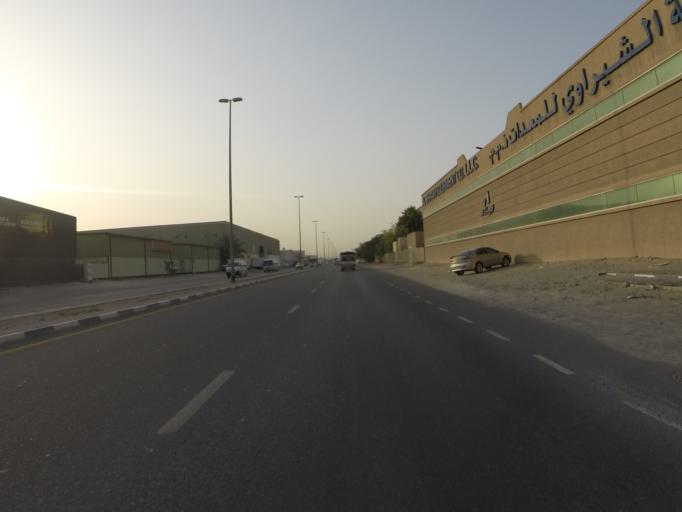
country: AE
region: Dubai
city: Dubai
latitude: 25.1338
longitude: 55.2266
